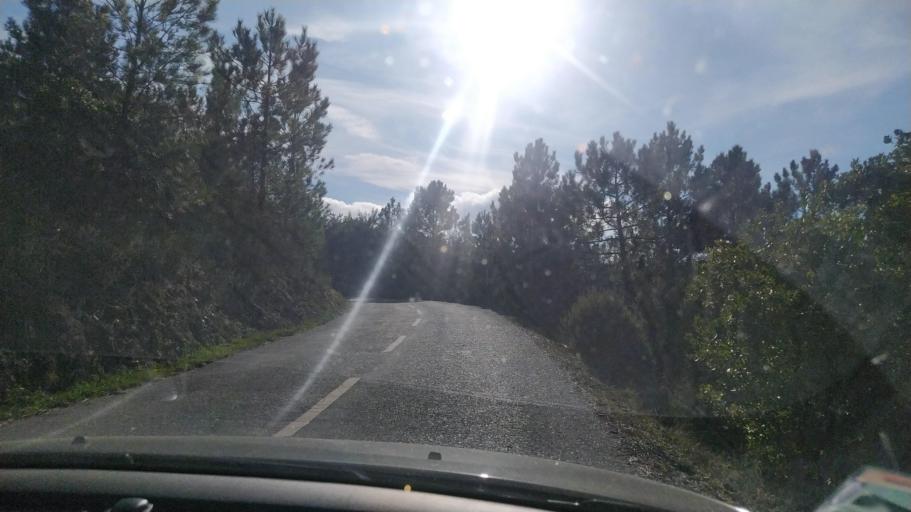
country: PT
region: Coimbra
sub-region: Oliveira do Hospital
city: Oliveira do Hospital
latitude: 40.2004
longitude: -7.7295
